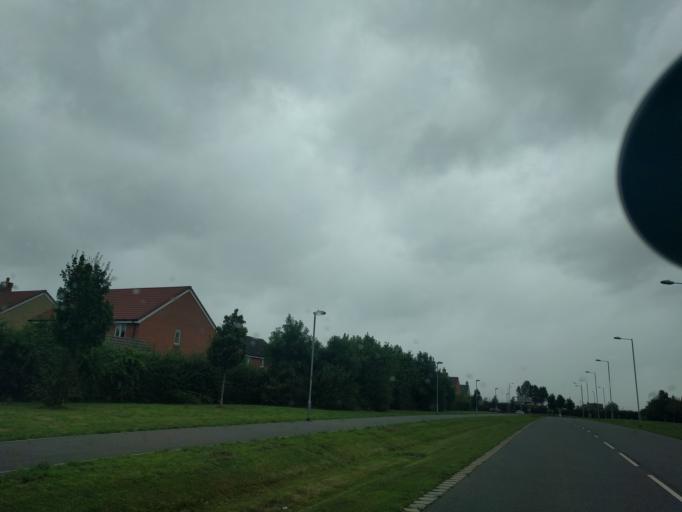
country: GB
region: England
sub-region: Wiltshire
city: Melksham
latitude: 51.3749
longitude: -2.1132
